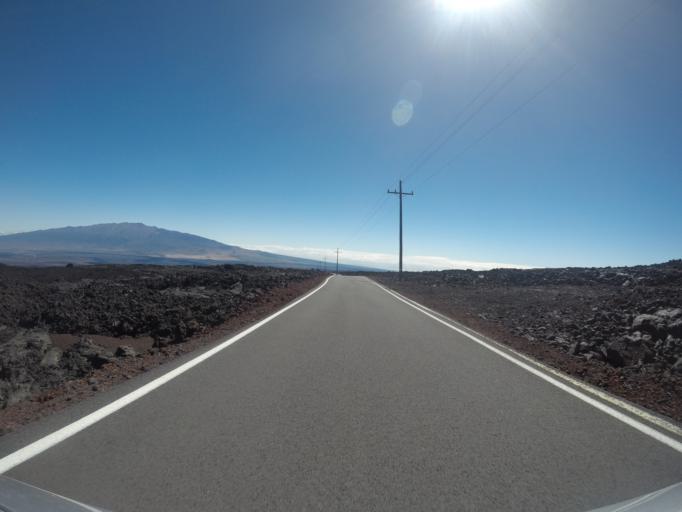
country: US
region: Hawaii
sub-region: Hawaii County
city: Volcano
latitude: 19.5560
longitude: -155.5351
